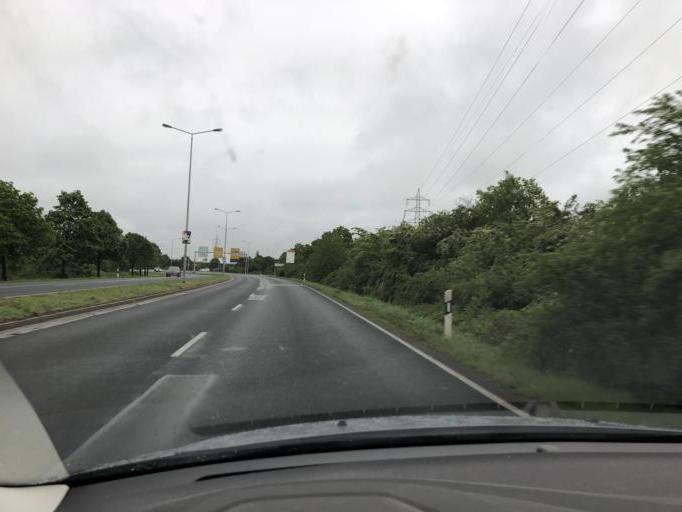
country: DE
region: Saxony-Anhalt
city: Dessau
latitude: 51.8093
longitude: 12.2210
